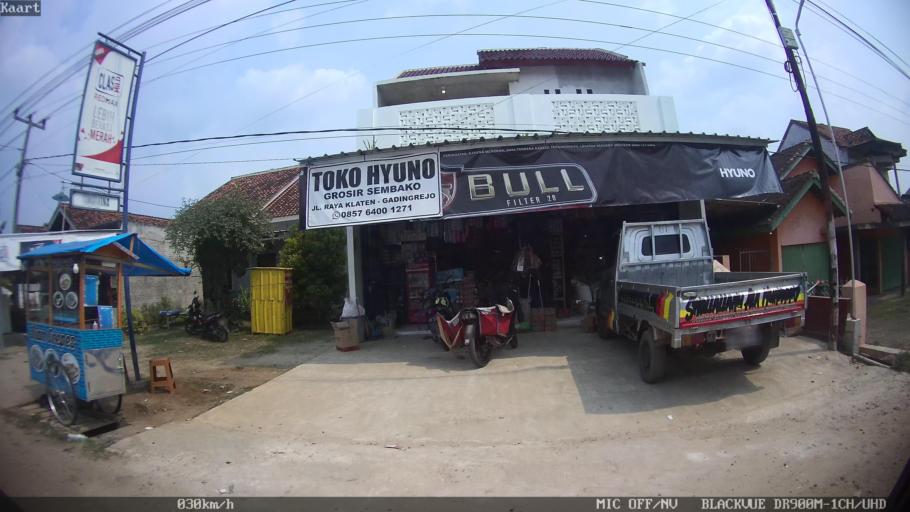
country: ID
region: Lampung
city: Gadingrejo
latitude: -5.3518
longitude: 105.0215
